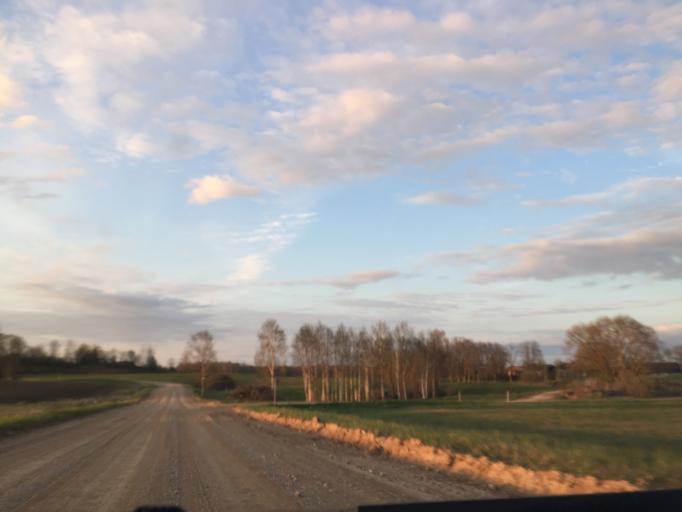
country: LV
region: Gulbenes Rajons
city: Gulbene
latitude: 57.2165
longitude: 26.7865
